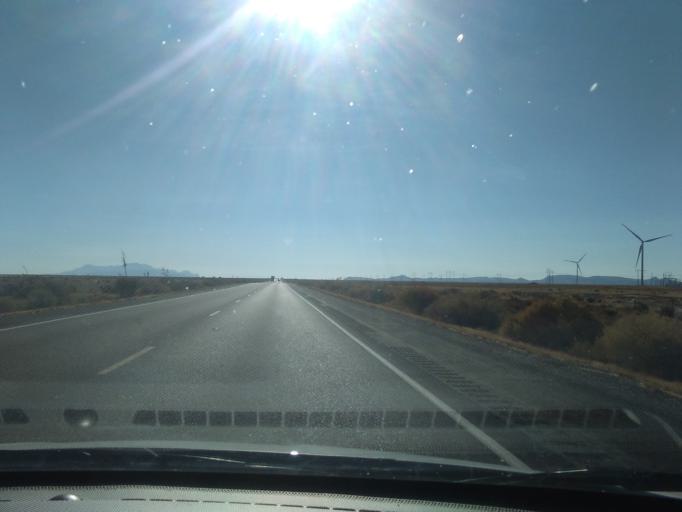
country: US
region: New Mexico
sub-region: Dona Ana County
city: Hatch
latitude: 32.5427
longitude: -107.4819
